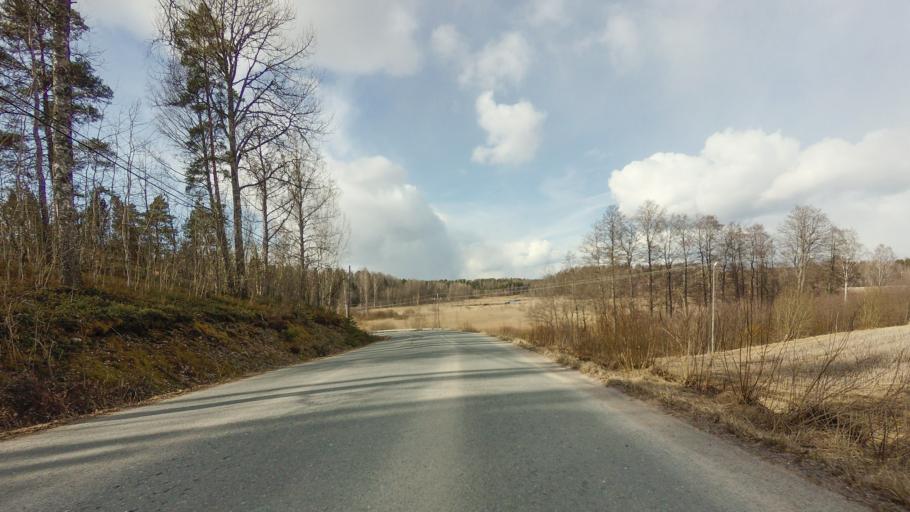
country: FI
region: Varsinais-Suomi
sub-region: Salo
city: Suomusjaervi
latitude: 60.3357
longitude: 23.7028
